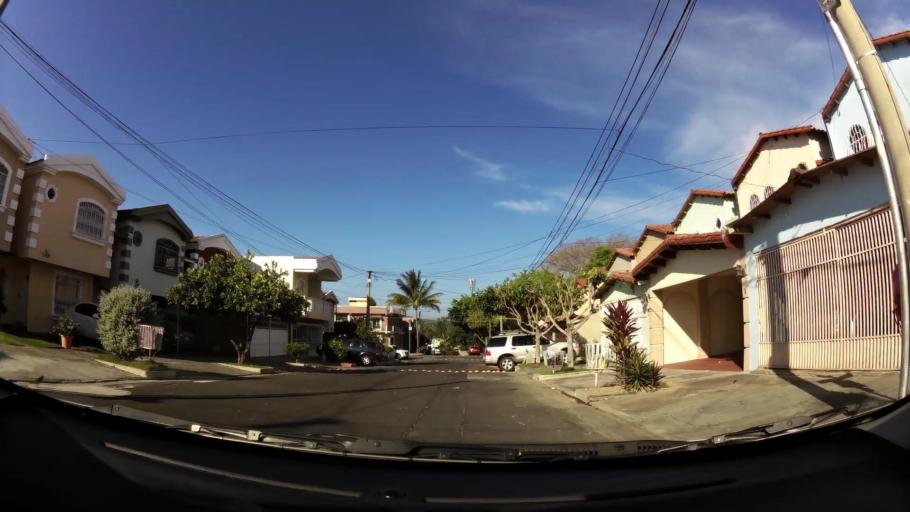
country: SV
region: La Libertad
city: Santa Tecla
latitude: 13.6827
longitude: -89.2894
